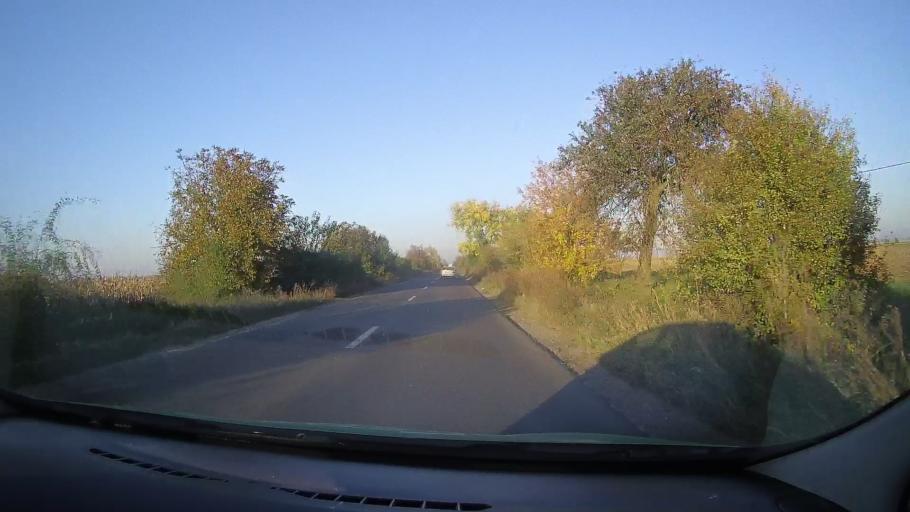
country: RO
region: Bihor
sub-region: Comuna Salard
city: Salard
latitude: 47.1939
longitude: 21.9990
